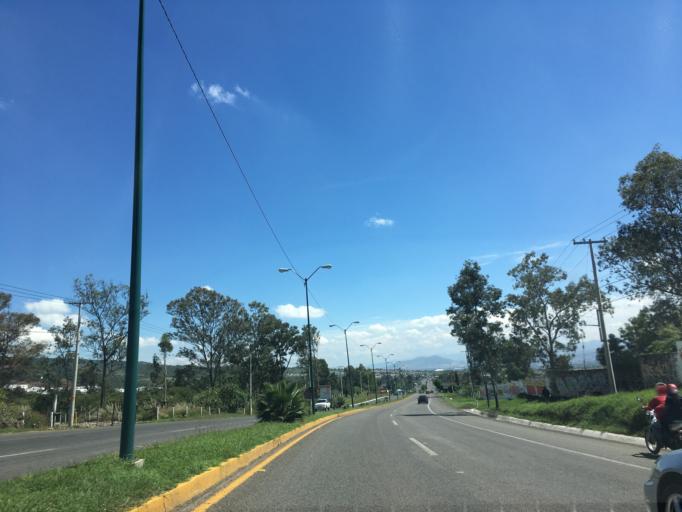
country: MX
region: Michoacan
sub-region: Morelia
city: Villa Magna
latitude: 19.6863
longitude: -101.3233
